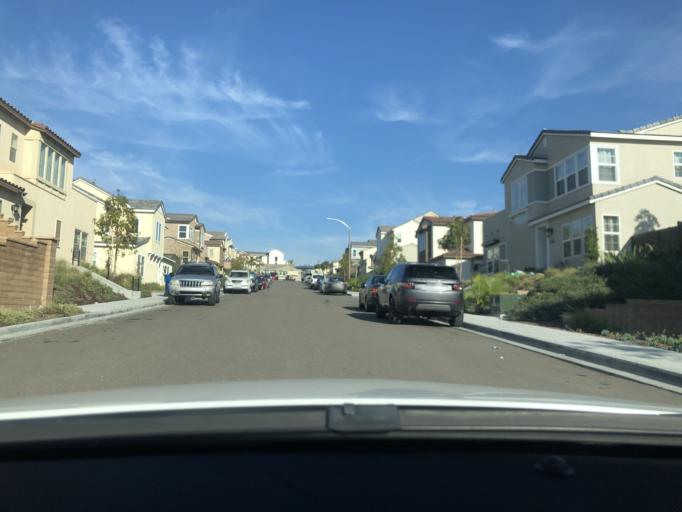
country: US
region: California
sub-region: San Diego County
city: Bonita
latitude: 32.5985
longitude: -117.0029
